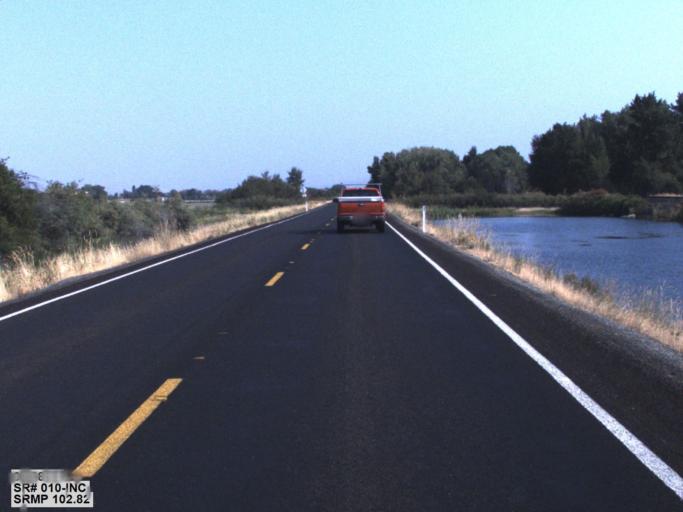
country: US
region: Washington
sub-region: Kittitas County
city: Ellensburg
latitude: 47.0512
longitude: -120.6351
